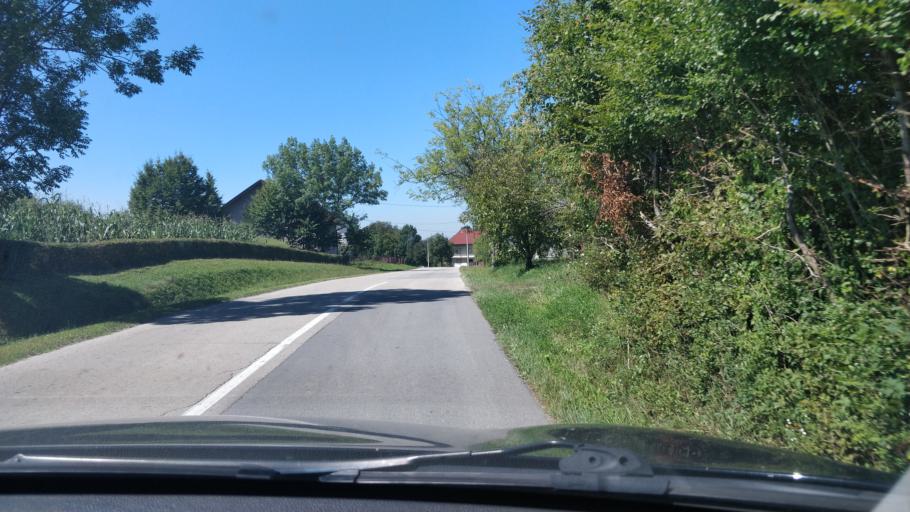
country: HR
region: Karlovacka
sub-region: Grad Karlovac
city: Karlovac
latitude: 45.4640
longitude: 15.6417
